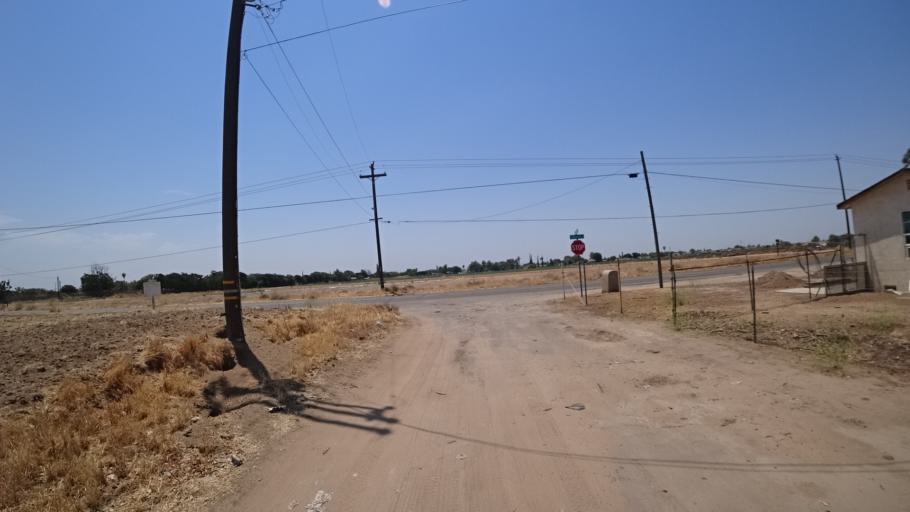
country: US
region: California
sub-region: Fresno County
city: West Park
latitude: 36.7143
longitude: -119.8123
